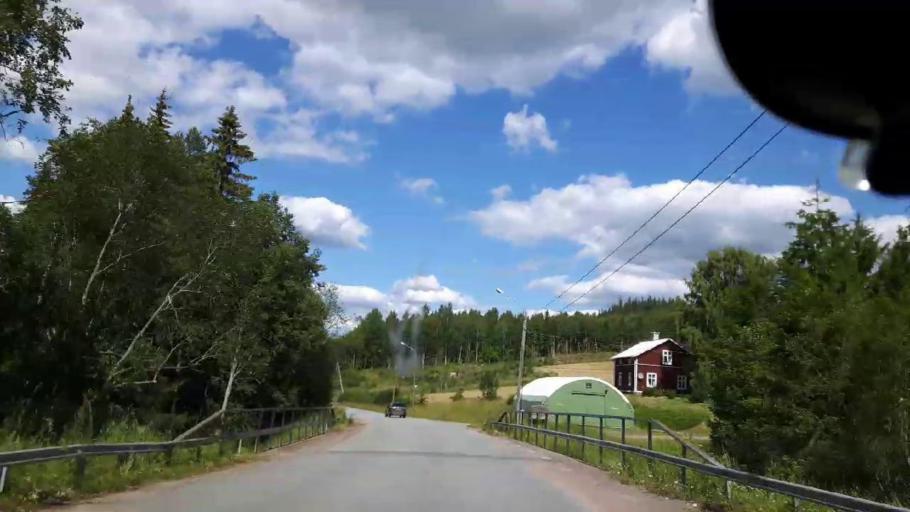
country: SE
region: Jaemtland
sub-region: Ragunda Kommun
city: Hammarstrand
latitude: 62.9420
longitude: 16.6922
